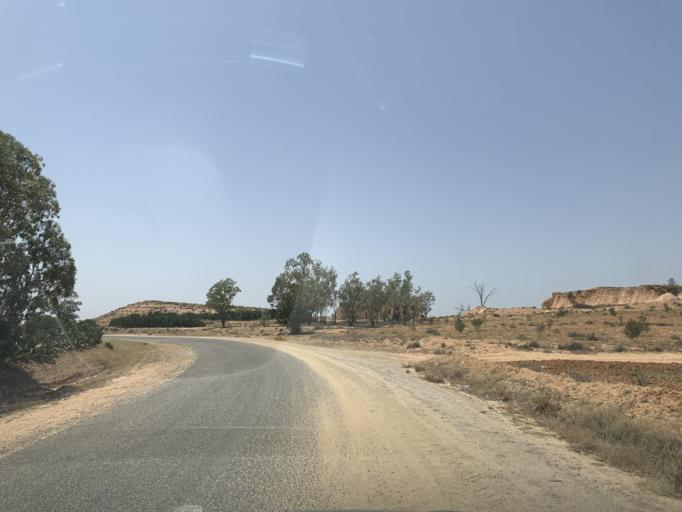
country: TN
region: Al Mahdiyah
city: Shurban
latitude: 35.1610
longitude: 10.2577
